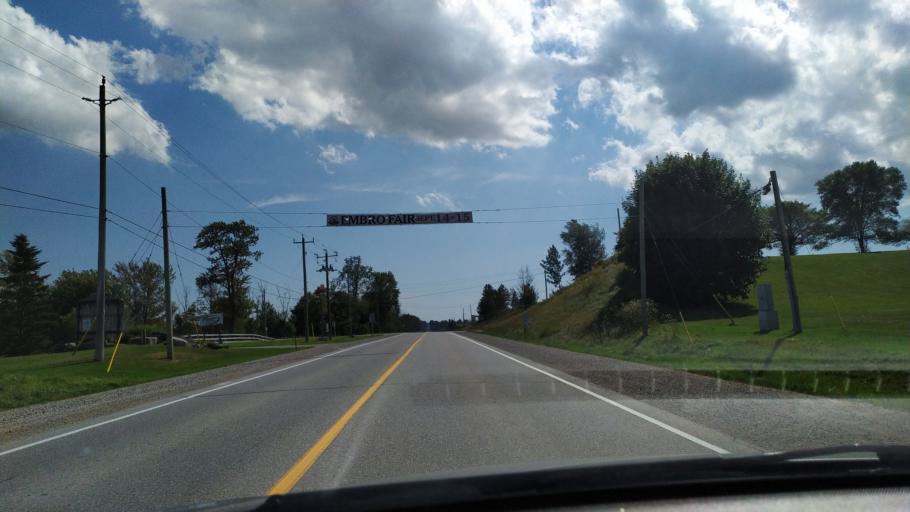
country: CA
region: Ontario
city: Ingersoll
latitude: 43.1505
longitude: -80.8986
